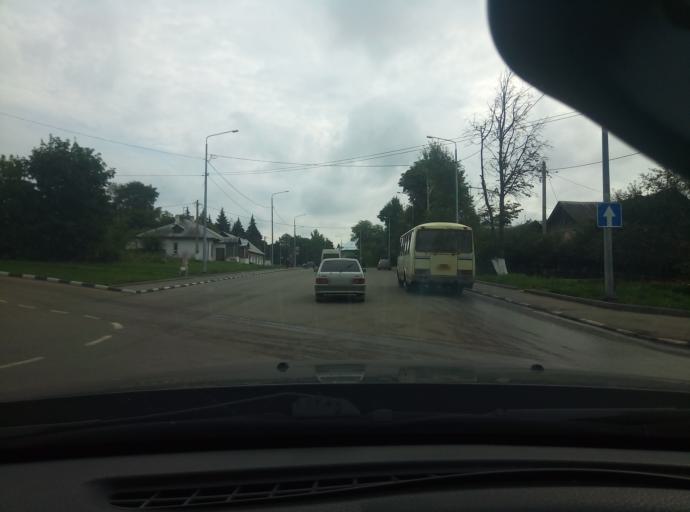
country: RU
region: Tula
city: Donskoy
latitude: 53.9679
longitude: 38.3314
